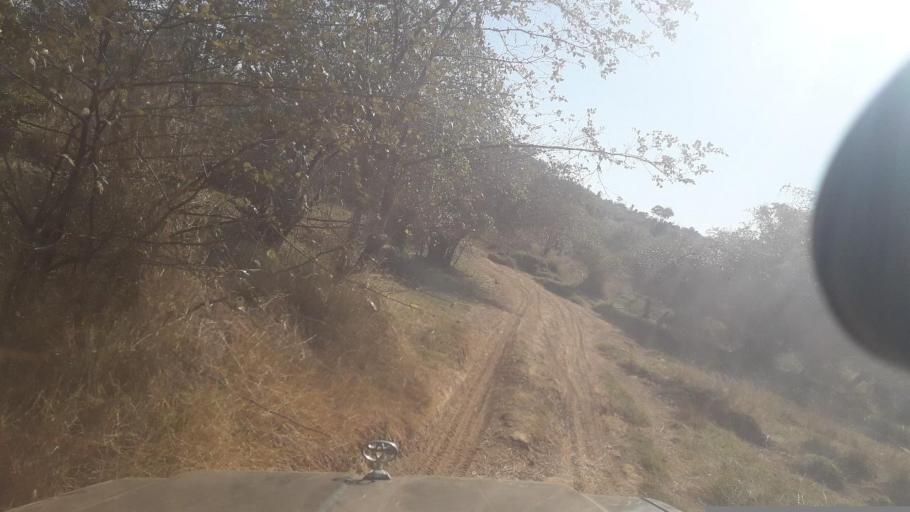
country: MG
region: Boeny
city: Sitampiky
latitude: -16.3761
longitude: 45.5901
